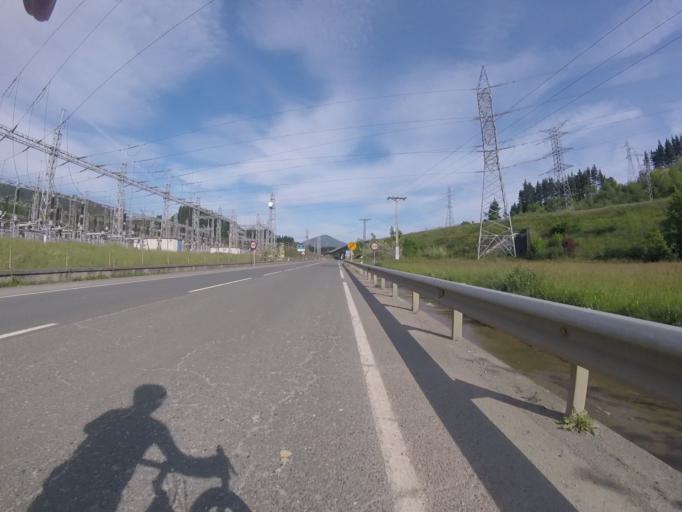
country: ES
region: Basque Country
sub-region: Provincia de Guipuzcoa
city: Gabiria
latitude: 43.0609
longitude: -2.2716
